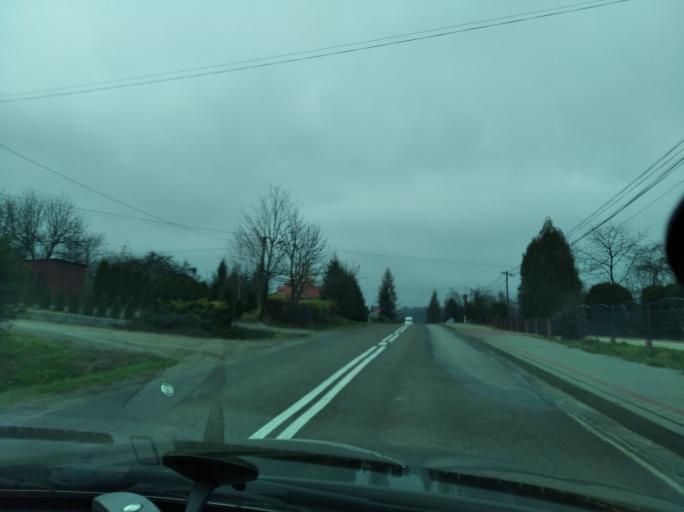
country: PL
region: Subcarpathian Voivodeship
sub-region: Powiat przeworski
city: Jawornik Polski
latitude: 49.8719
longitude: 22.2461
